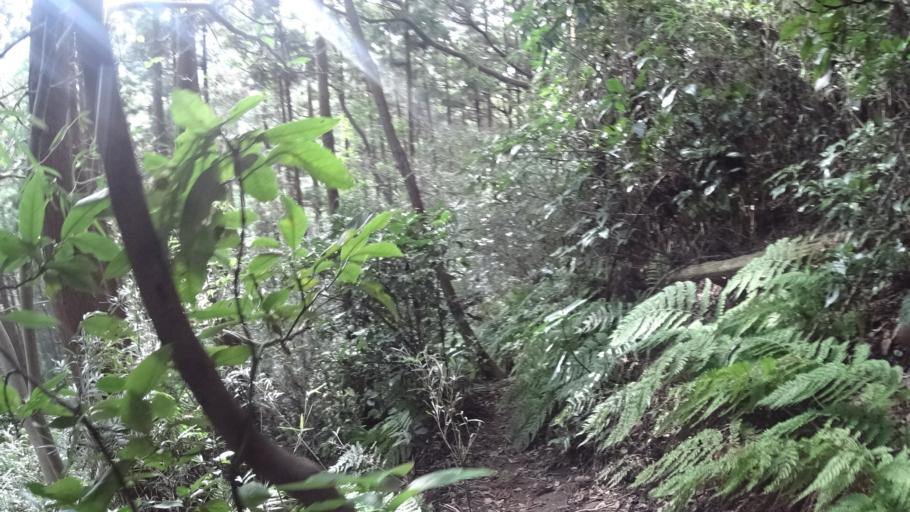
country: JP
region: Kanagawa
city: Hayama
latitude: 35.2841
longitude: 139.5966
